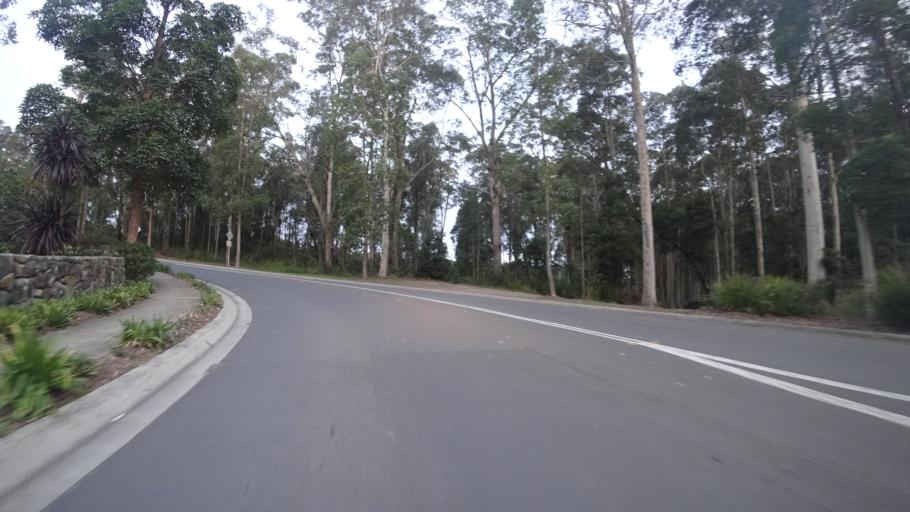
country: AU
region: New South Wales
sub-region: Shoalhaven Shire
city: Falls Creek
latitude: -35.0884
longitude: 150.6405
